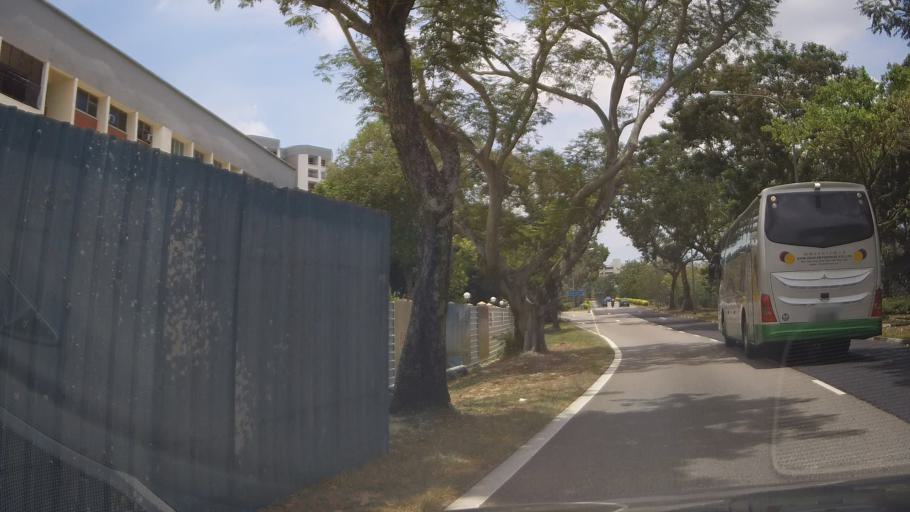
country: SG
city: Singapore
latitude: 1.3440
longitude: 103.9455
